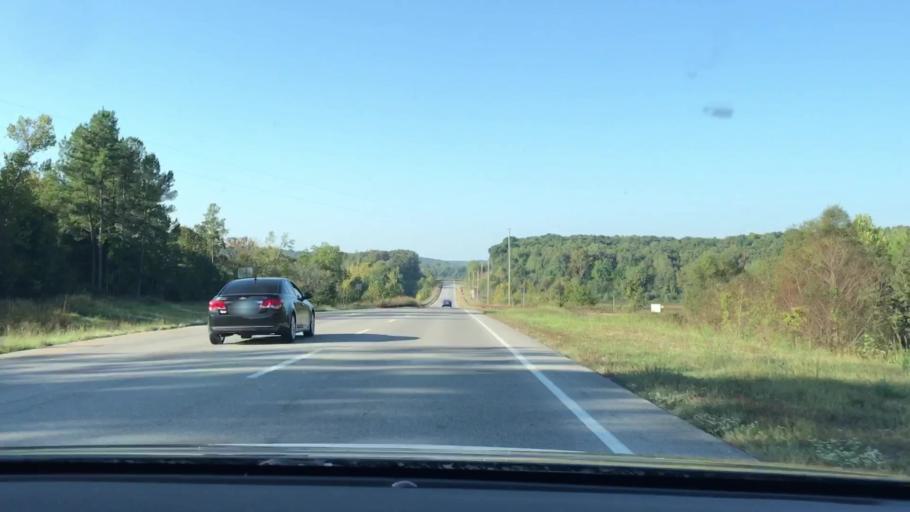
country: US
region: Kentucky
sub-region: Trigg County
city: Cadiz
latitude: 36.7990
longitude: -87.9972
